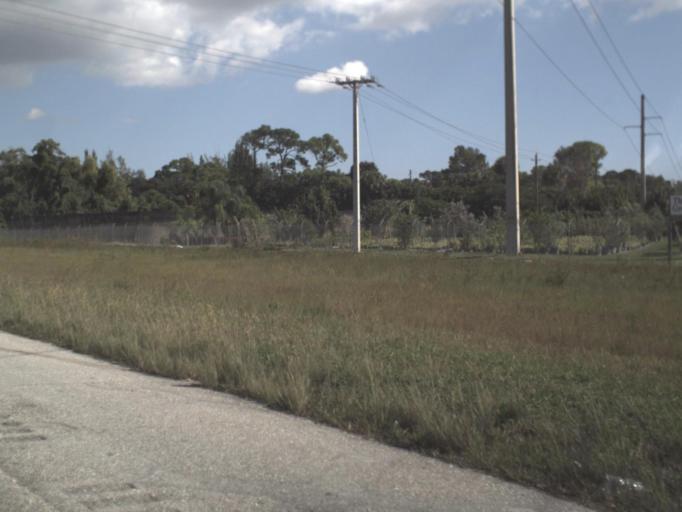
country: US
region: Florida
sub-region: Palm Beach County
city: Lake Belvedere Estates
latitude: 26.6750
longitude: -80.1693
